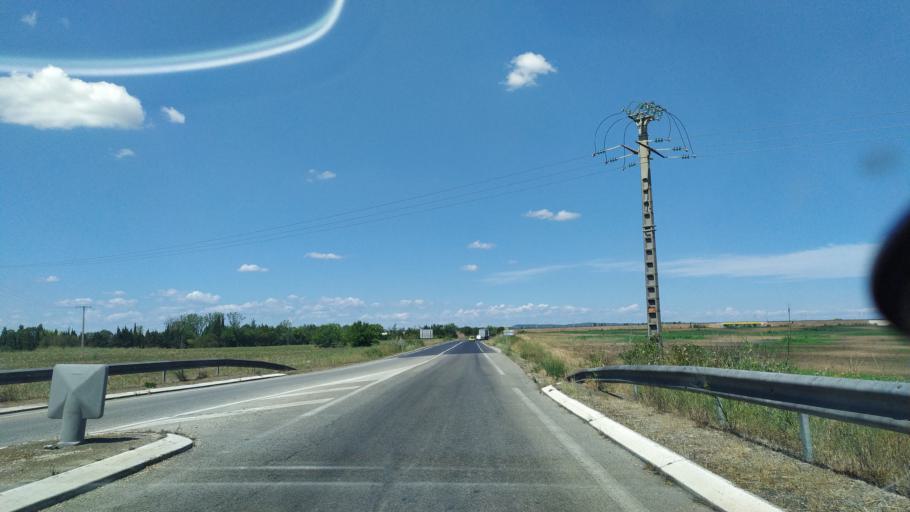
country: FR
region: Languedoc-Roussillon
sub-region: Departement du Gard
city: Vauvert
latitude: 43.7176
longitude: 4.2712
